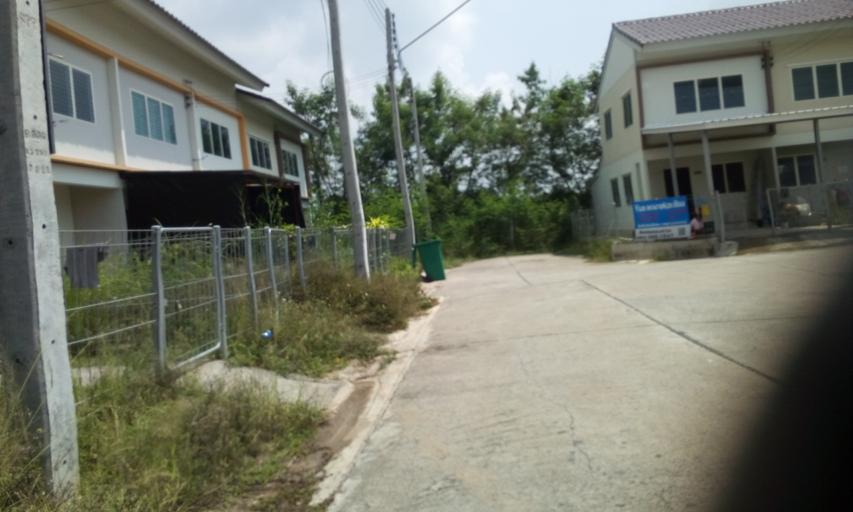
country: TH
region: Pathum Thani
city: Nong Suea
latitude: 14.0641
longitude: 100.8226
